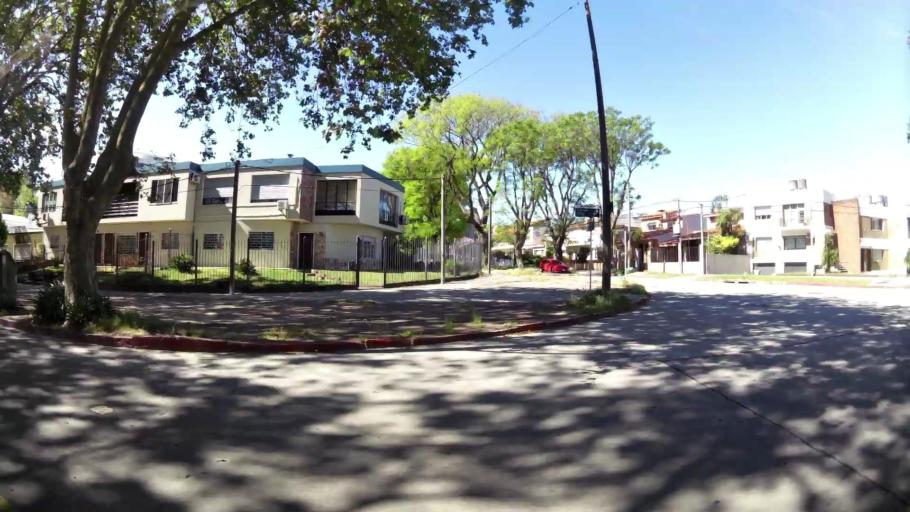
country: UY
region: Canelones
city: Paso de Carrasco
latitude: -34.8888
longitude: -56.1019
